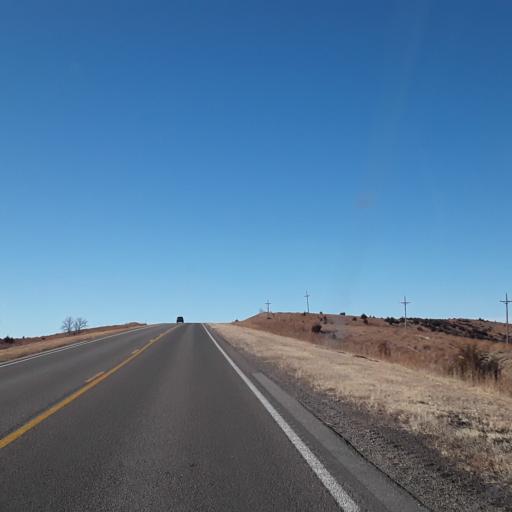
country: US
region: Nebraska
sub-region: Frontier County
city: Stockville
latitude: 40.6286
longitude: -100.5398
